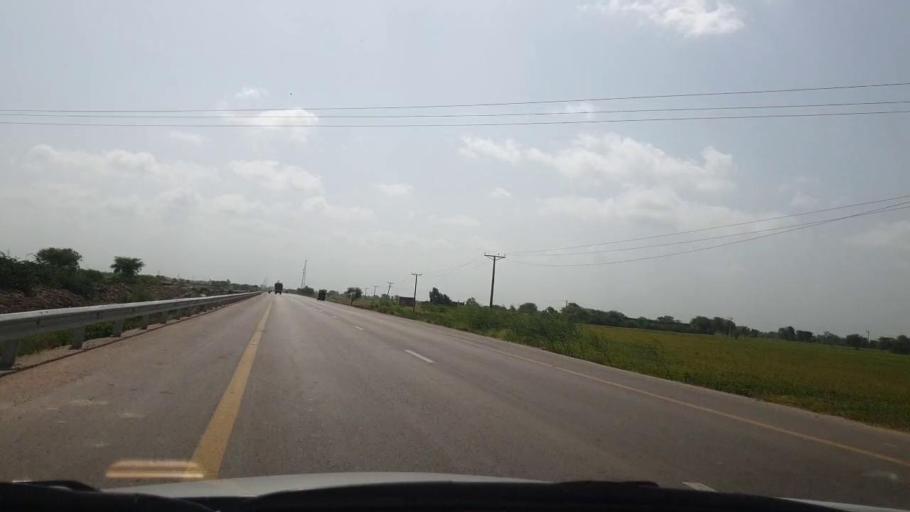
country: PK
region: Sindh
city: Matli
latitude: 24.9619
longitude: 68.6833
